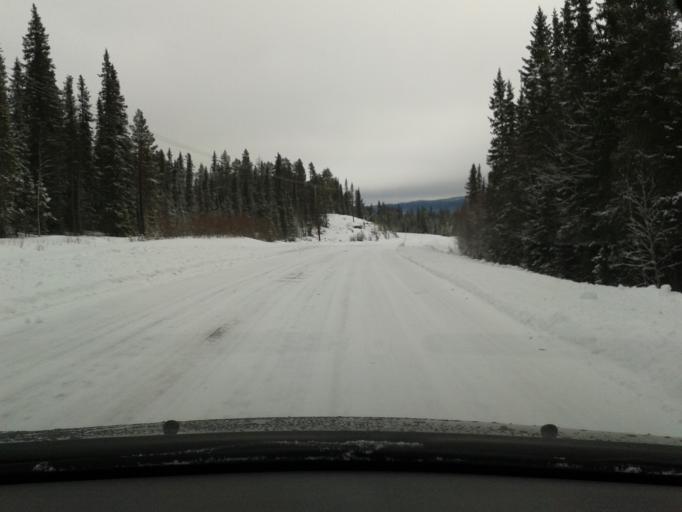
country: SE
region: Vaesterbotten
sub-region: Vilhelmina Kommun
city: Sjoberg
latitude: 65.2363
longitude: 15.8339
